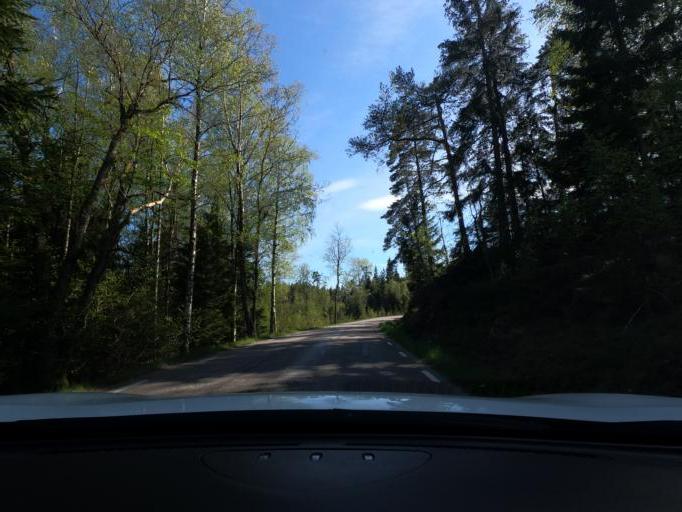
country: SE
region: Vaestra Goetaland
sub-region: Harryda Kommun
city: Hindas
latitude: 57.6661
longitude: 12.3533
